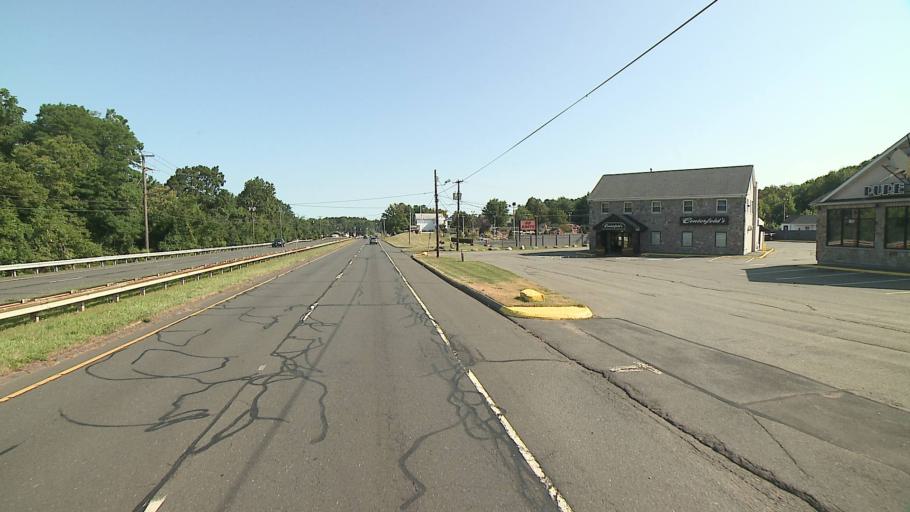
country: US
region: Connecticut
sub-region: Hartford County
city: Kensington
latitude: 41.6011
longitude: -72.7532
